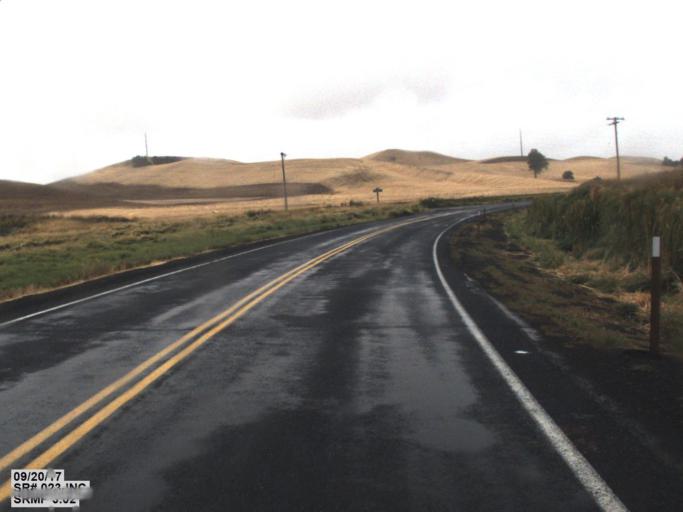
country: US
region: Washington
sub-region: Whitman County
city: Colfax
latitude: 47.0005
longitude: -117.4151
